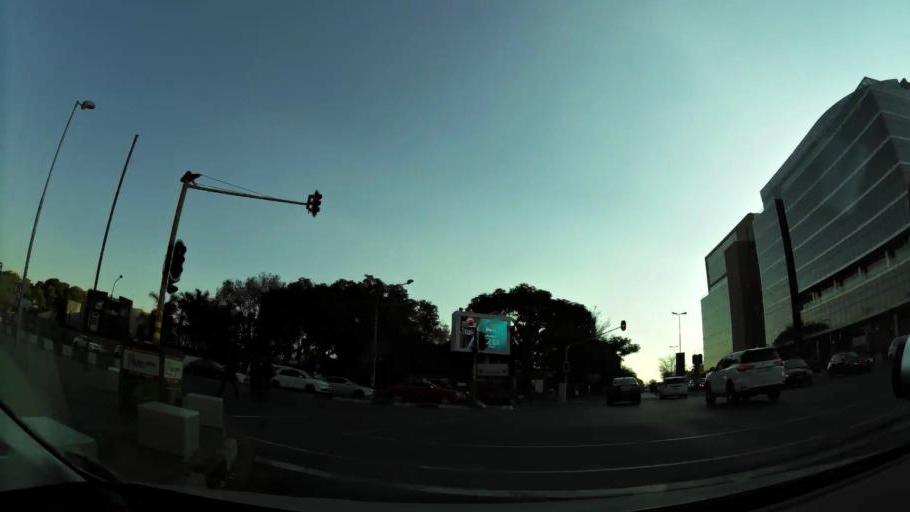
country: ZA
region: Gauteng
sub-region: City of Johannesburg Metropolitan Municipality
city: Johannesburg
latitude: -26.1498
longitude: 28.0455
